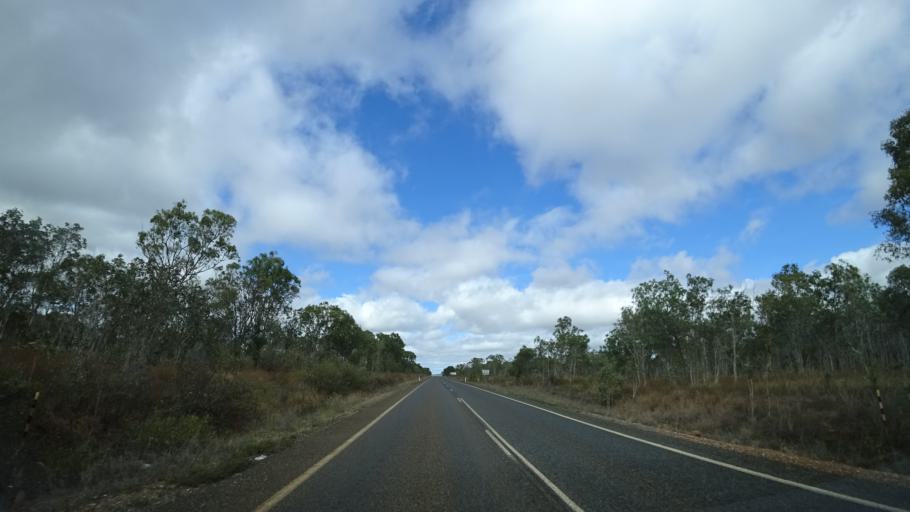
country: AU
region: Queensland
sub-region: Cook
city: Cooktown
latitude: -15.8784
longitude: 144.8603
